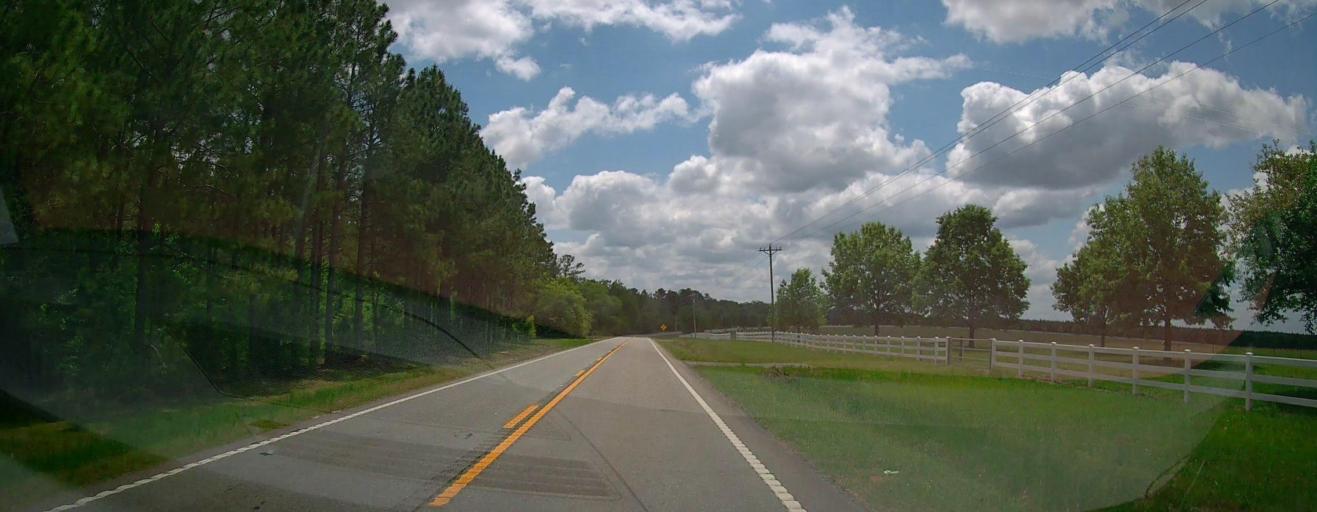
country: US
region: Georgia
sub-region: Laurens County
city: Dublin
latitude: 32.5908
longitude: -83.0131
